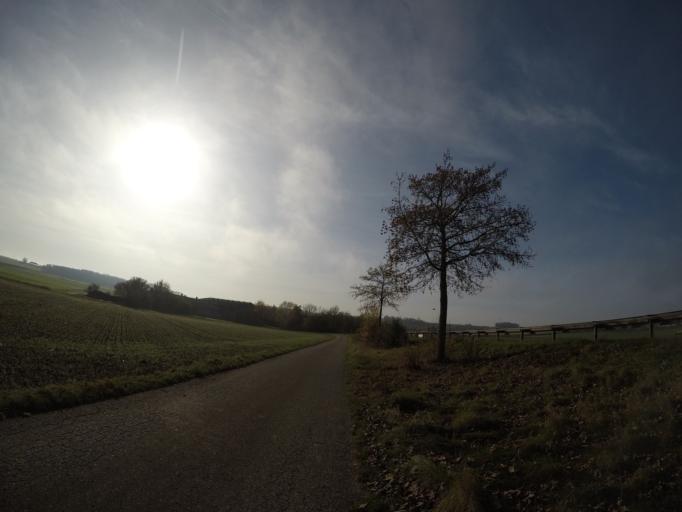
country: DE
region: Baden-Wuerttemberg
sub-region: Tuebingen Region
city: Langenau
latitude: 48.4884
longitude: 10.0727
